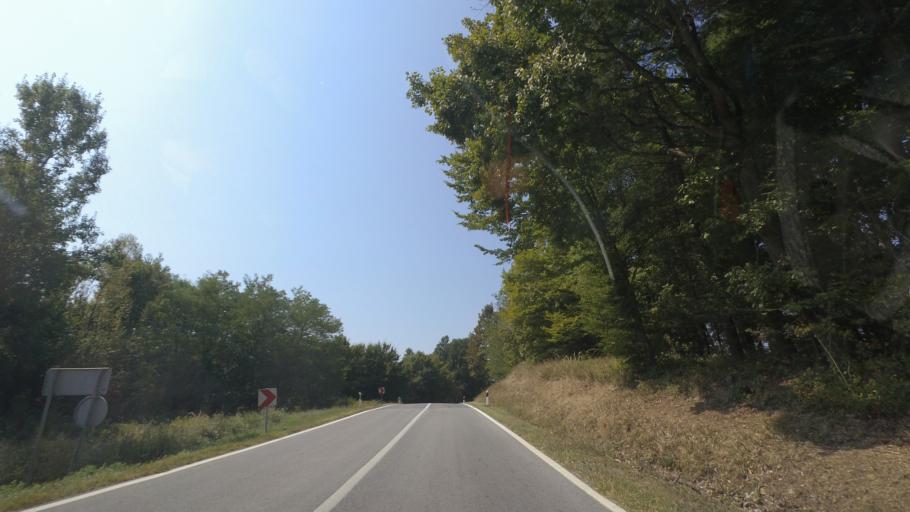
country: HR
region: Pozesko-Slavonska
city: Lipik
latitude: 45.4105
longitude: 17.0710
